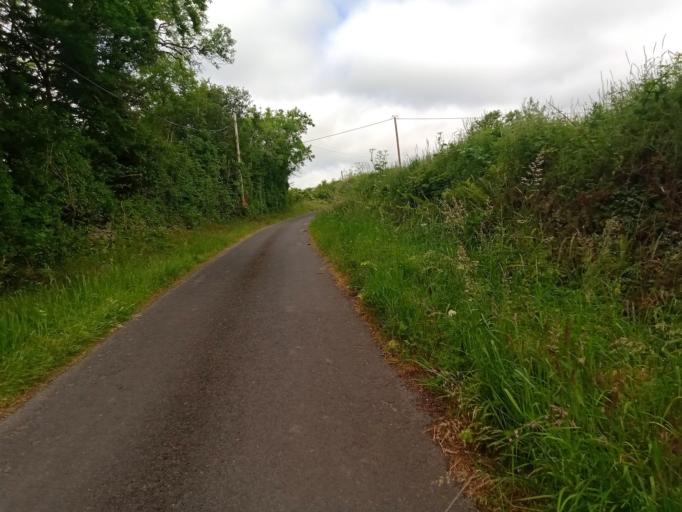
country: IE
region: Leinster
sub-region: Laois
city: Rathdowney
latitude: 52.7741
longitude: -7.4683
